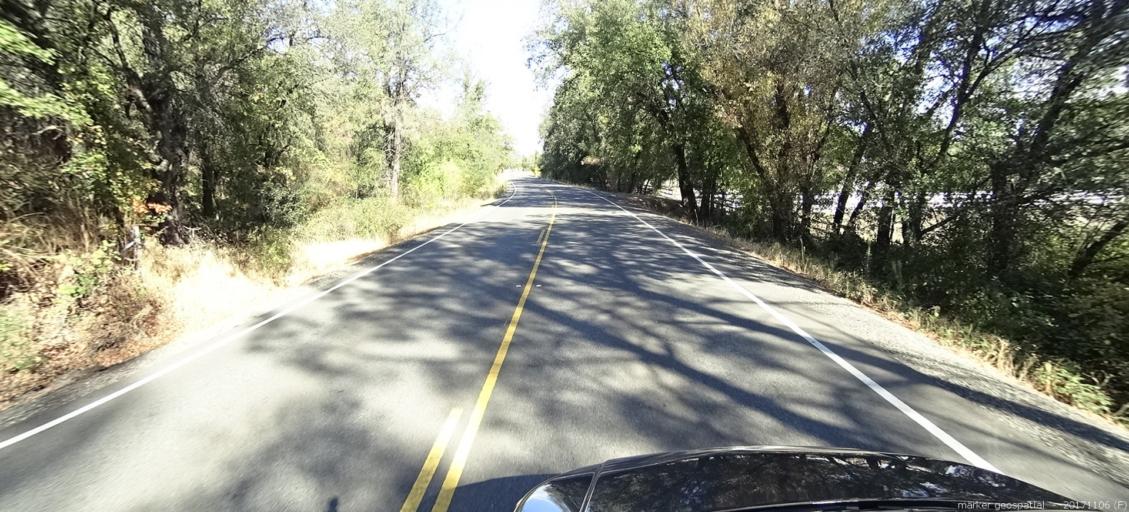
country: US
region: California
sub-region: Shasta County
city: Bella Vista
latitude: 40.6208
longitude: -122.2333
